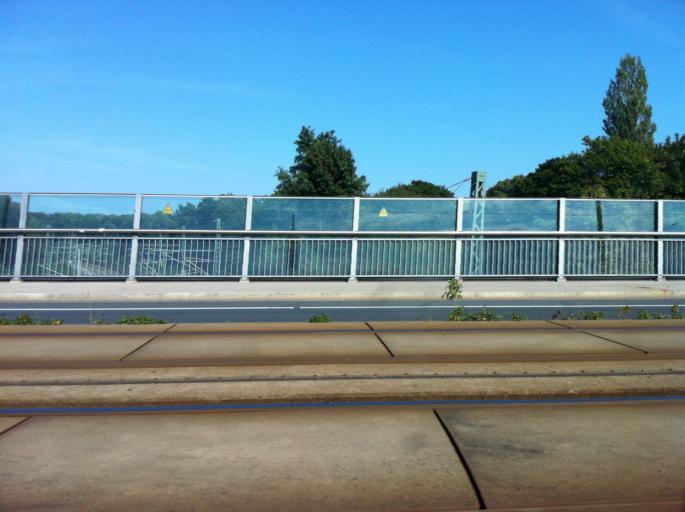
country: DE
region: Saxony
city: Leipzig
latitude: 51.3118
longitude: 12.3956
